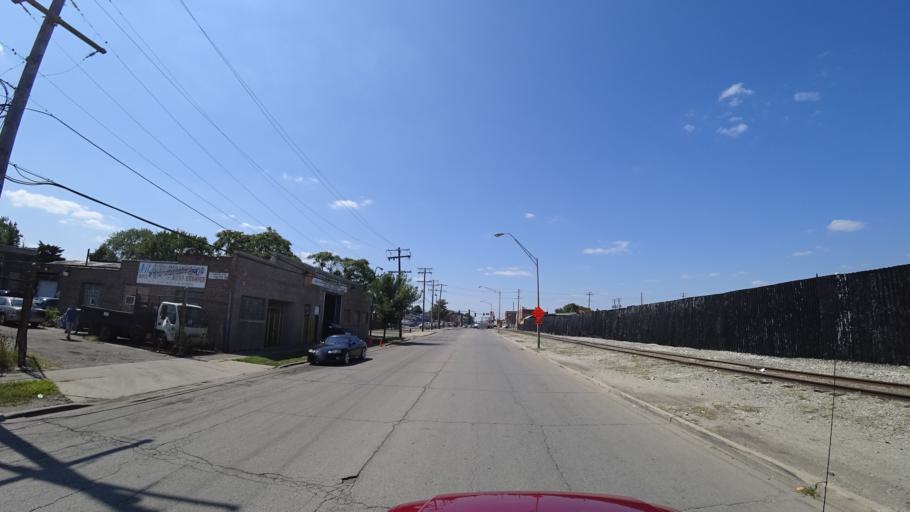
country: US
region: Illinois
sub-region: Cook County
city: Cicero
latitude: 41.8586
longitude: -87.7427
